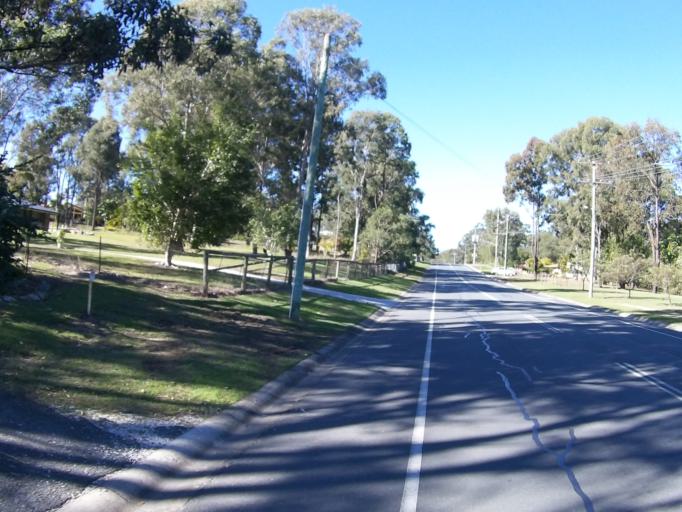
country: AU
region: Queensland
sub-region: Logan
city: Windaroo
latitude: -27.7558
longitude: 153.2018
